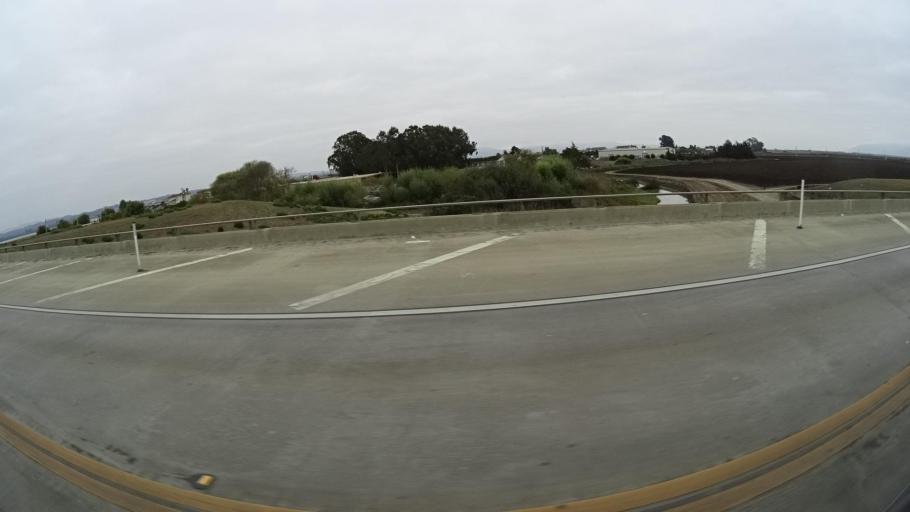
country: US
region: California
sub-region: Monterey County
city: Castroville
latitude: 36.7680
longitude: -121.7668
